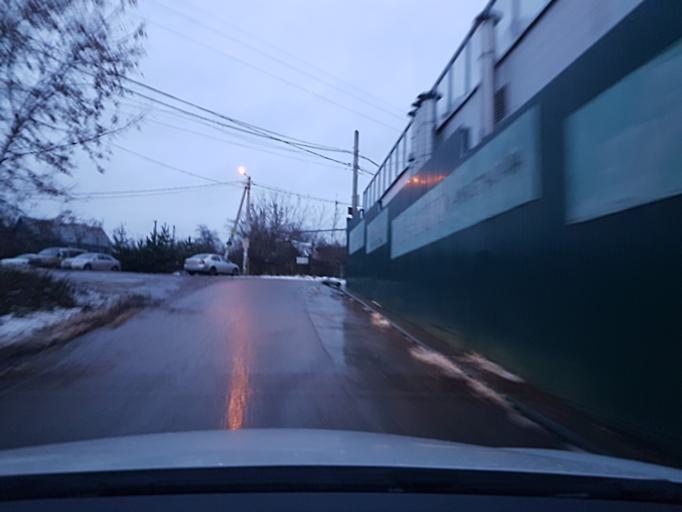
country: RU
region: Moskovskaya
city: Sheremet'yevskiy
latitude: 55.9869
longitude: 37.5200
